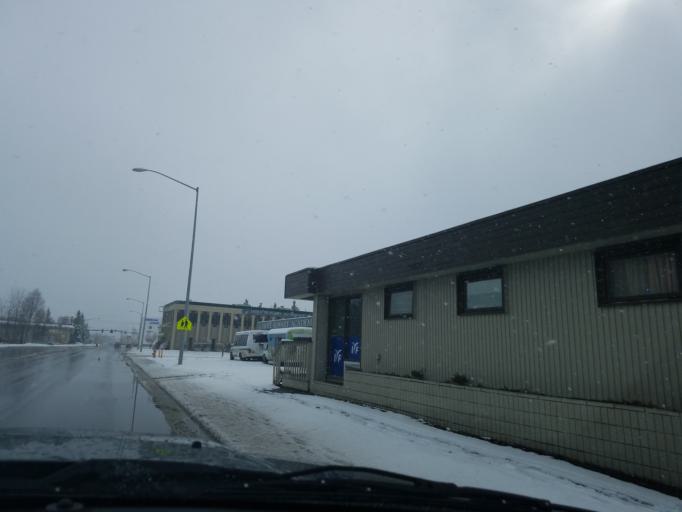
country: US
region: Alaska
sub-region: Anchorage Municipality
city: Anchorage
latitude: 61.1988
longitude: -149.9023
